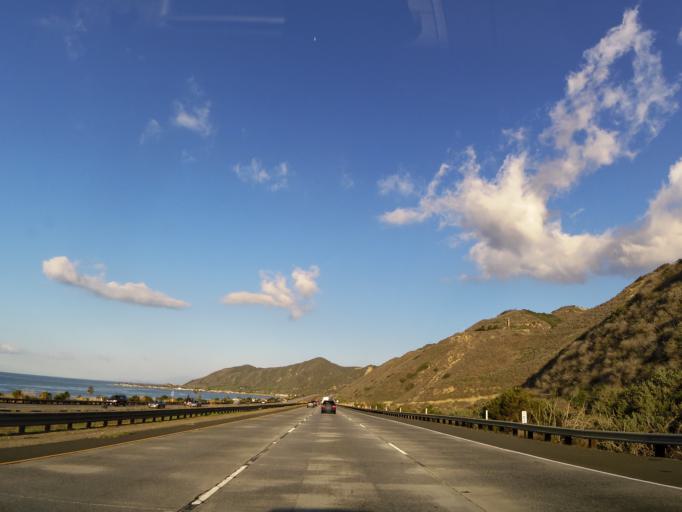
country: US
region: California
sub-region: Ventura County
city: Ventura
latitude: 34.3092
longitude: -119.3524
